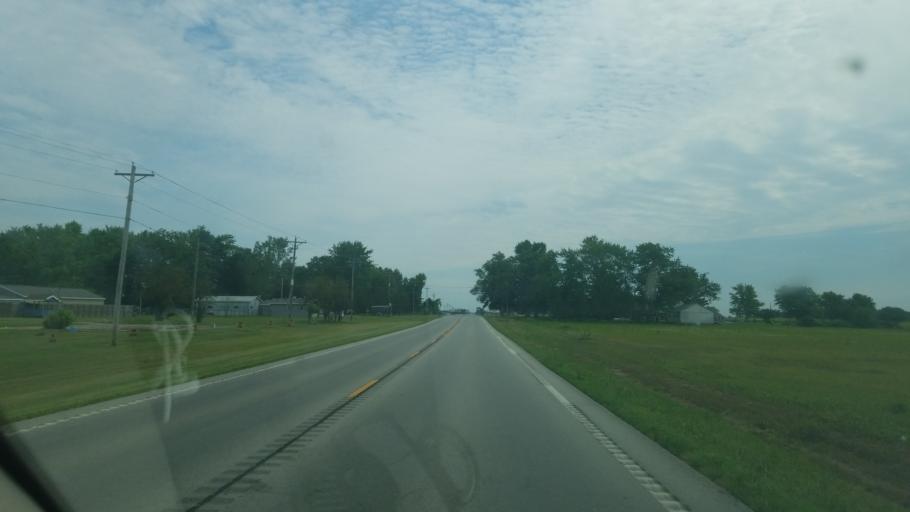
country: US
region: Ohio
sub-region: Seneca County
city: Fostoria
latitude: 41.1279
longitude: -83.4754
